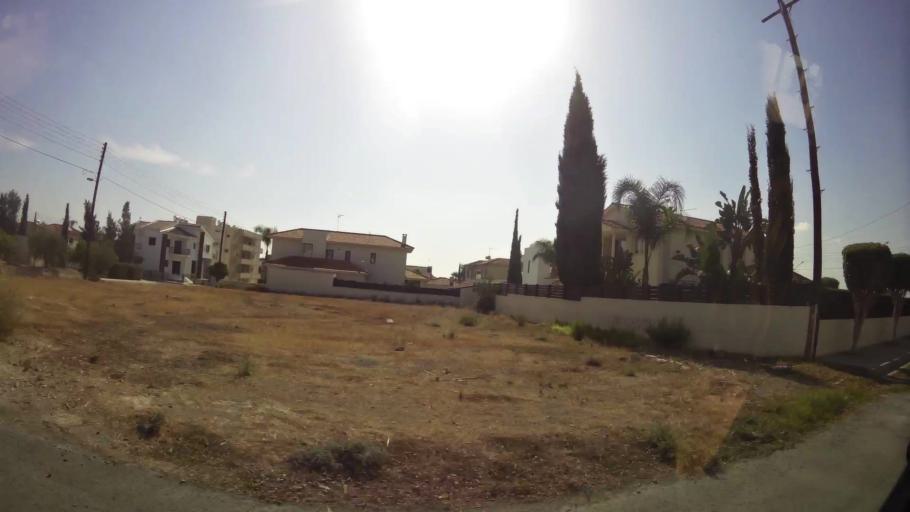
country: CY
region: Larnaka
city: Aradippou
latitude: 34.9441
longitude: 33.5819
